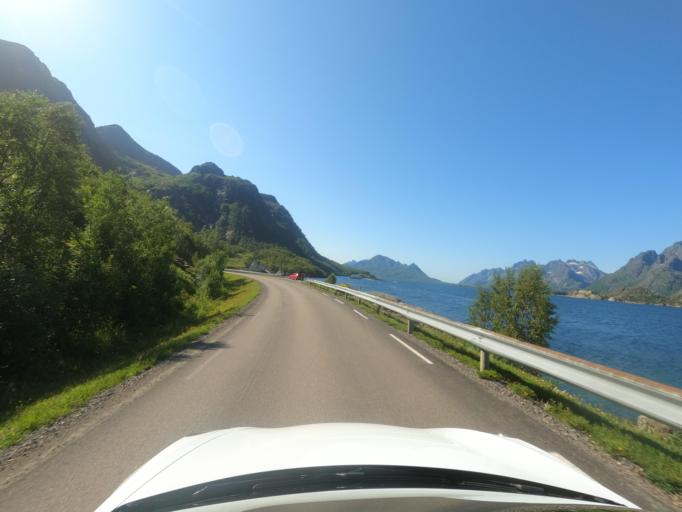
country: NO
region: Nordland
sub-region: Hadsel
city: Stokmarknes
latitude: 68.3458
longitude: 15.0515
